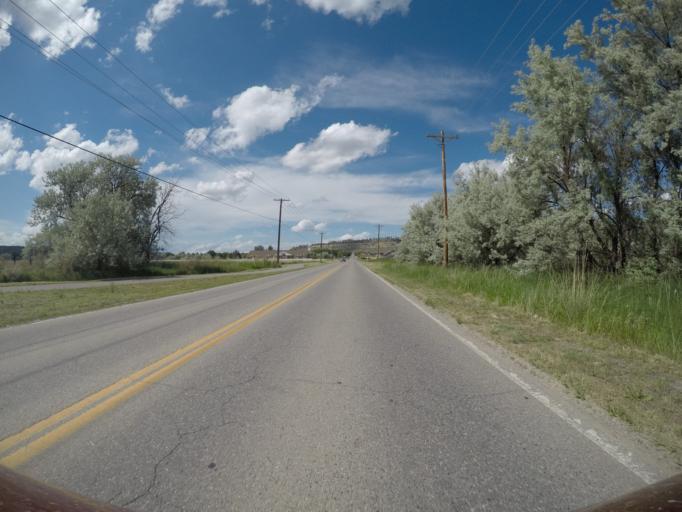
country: US
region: Montana
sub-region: Yellowstone County
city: Billings
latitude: 45.7942
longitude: -108.6527
